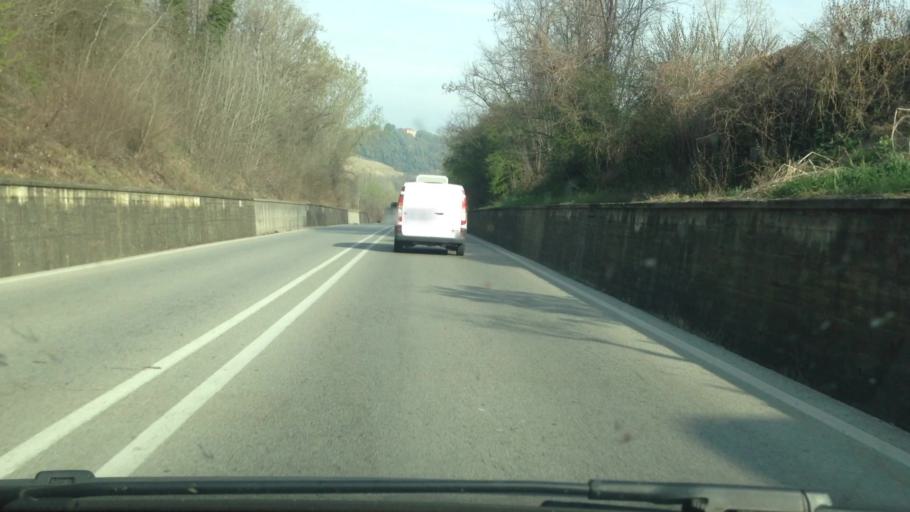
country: IT
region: Piedmont
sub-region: Provincia di Cuneo
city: Canale
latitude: 44.7973
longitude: 7.9833
